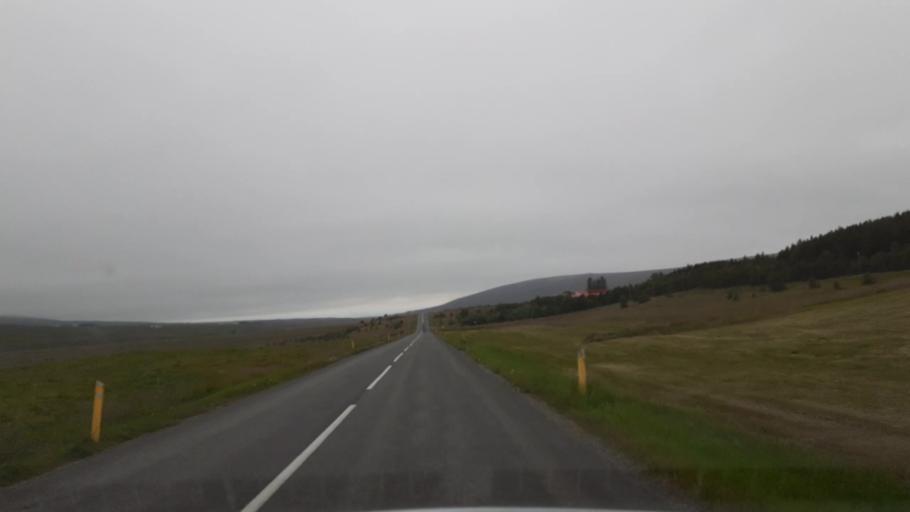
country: IS
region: Northeast
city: Siglufjoerdur
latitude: 65.7341
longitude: -19.1182
